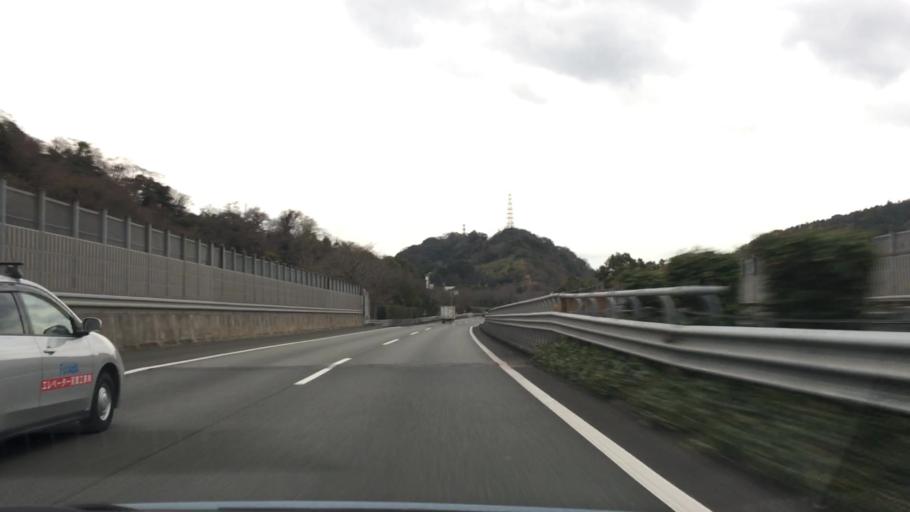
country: JP
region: Shizuoka
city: Fuji
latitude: 35.1367
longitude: 138.6147
